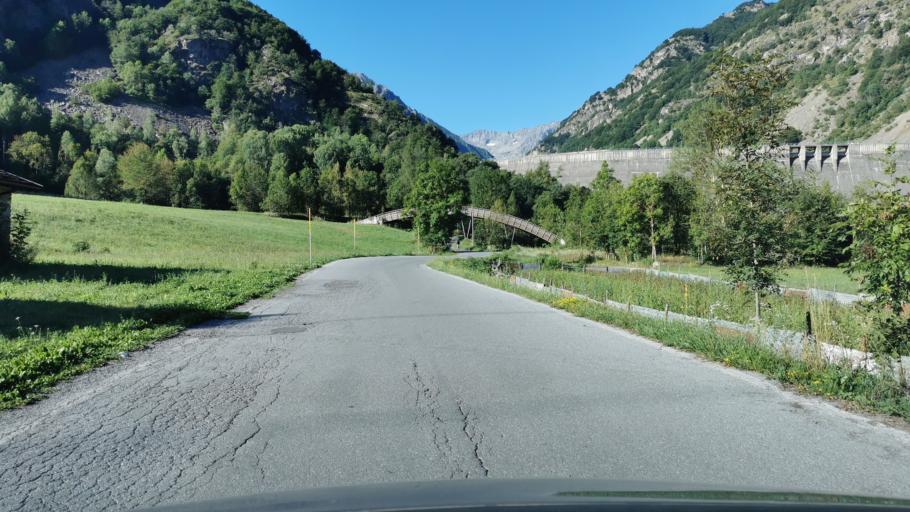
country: IT
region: Piedmont
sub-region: Provincia di Cuneo
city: Entracque
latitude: 44.2278
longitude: 7.3951
